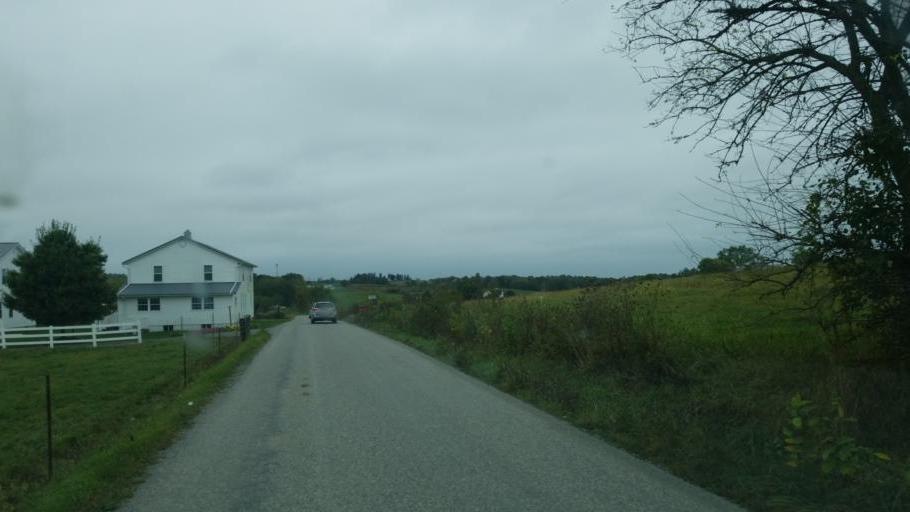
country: US
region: Ohio
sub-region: Wayne County
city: Apple Creek
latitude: 40.6533
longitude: -81.8081
